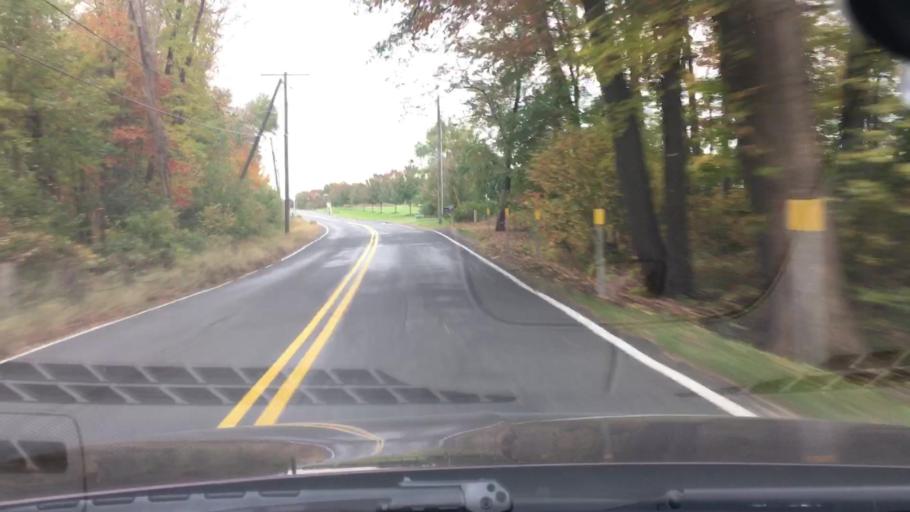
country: US
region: Connecticut
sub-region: Tolland County
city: Somers
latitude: 42.0087
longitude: -72.4812
